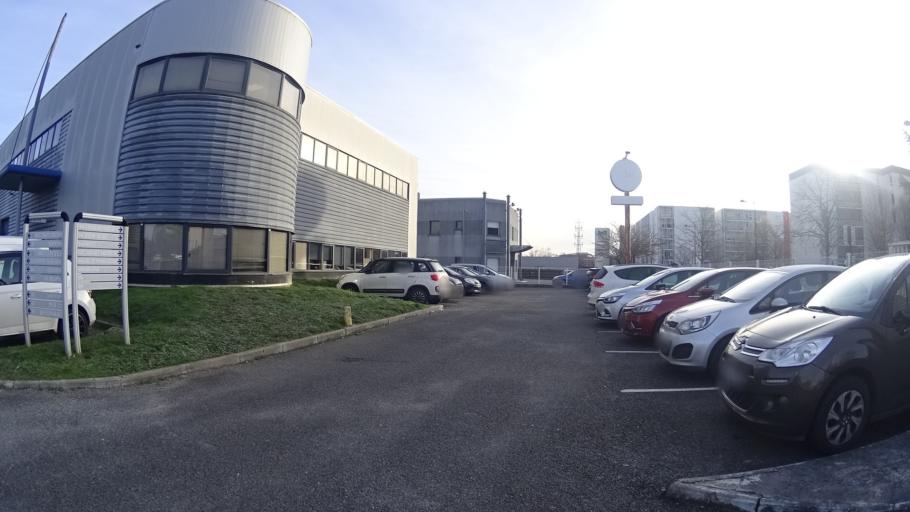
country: FR
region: Aquitaine
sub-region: Departement de la Gironde
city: Artigues-pres-Bordeaux
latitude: 44.8520
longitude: -0.5111
